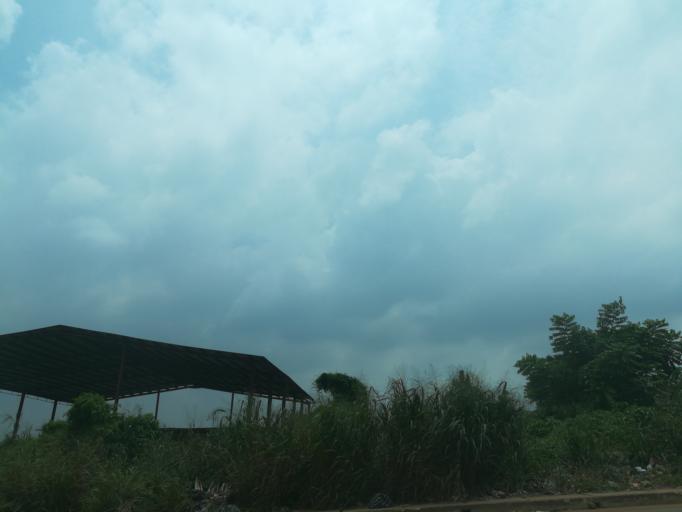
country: NG
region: Lagos
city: Ikorodu
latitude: 6.6291
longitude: 3.5315
